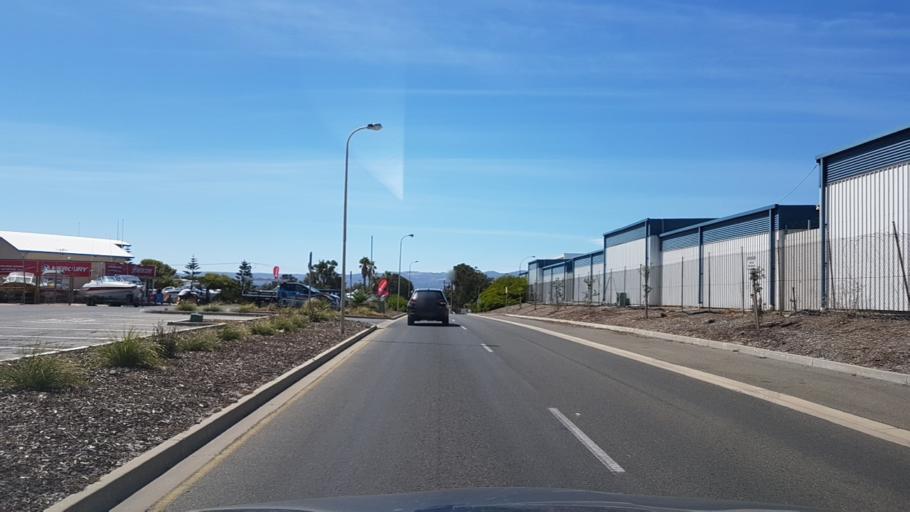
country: AU
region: South Australia
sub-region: Adelaide
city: Glenelg
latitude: -34.9585
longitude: 138.5080
